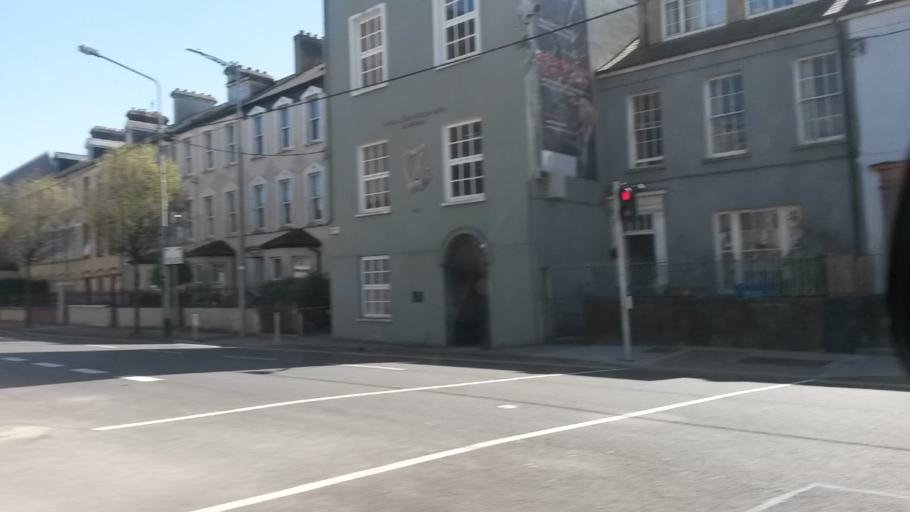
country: IE
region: Munster
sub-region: County Cork
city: Cork
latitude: 51.8980
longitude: -8.4827
